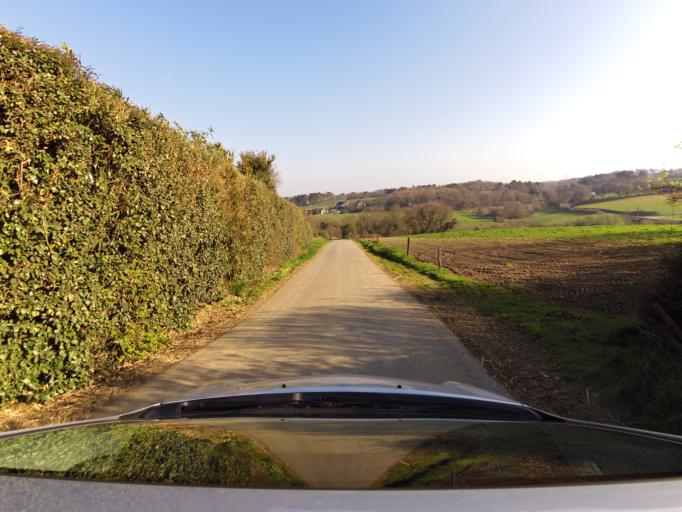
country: FR
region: Brittany
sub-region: Departement du Morbihan
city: Guidel-Plage
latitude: 47.7741
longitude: -3.4921
